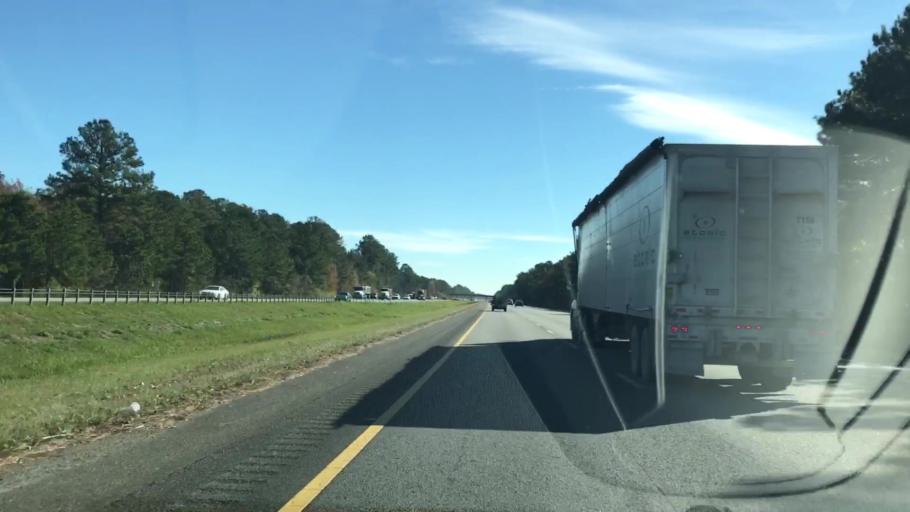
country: US
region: South Carolina
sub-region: Berkeley County
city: Sangaree
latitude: 33.0237
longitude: -80.1329
